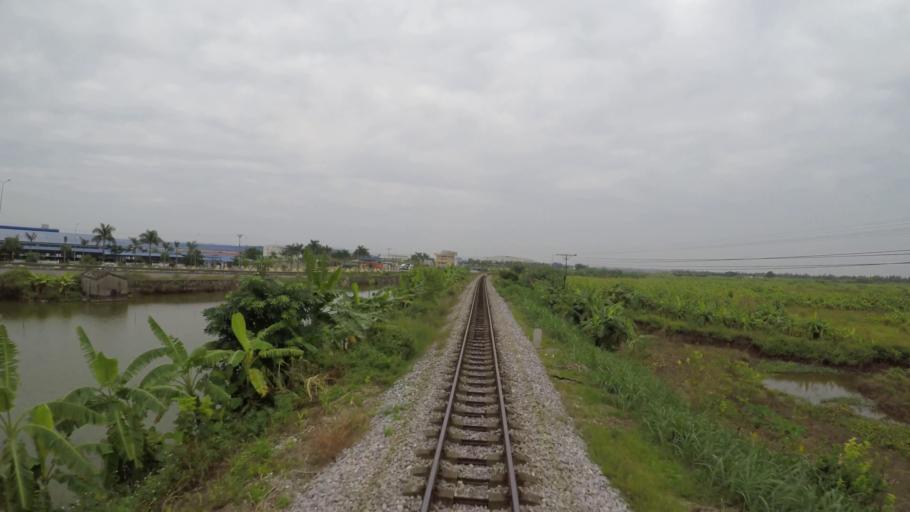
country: VN
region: Hai Duong
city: Nam Sach
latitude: 20.9754
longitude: 106.3954
